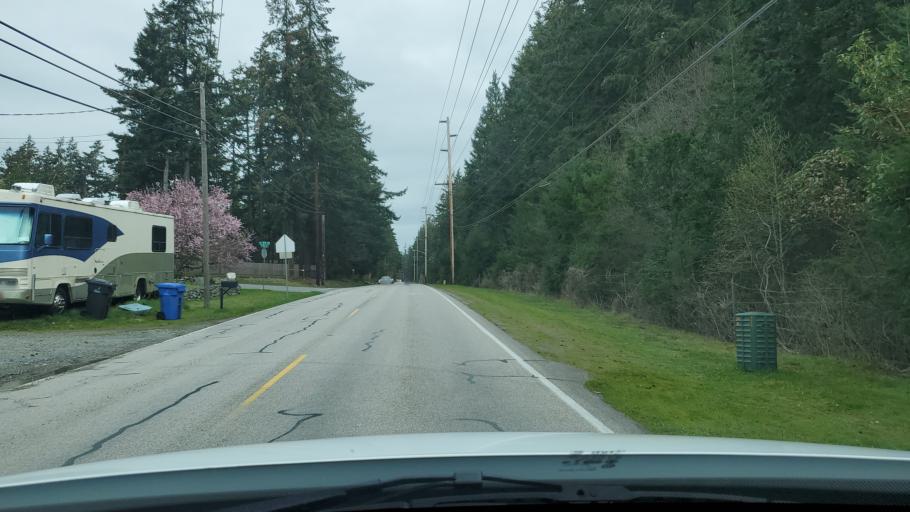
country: US
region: Washington
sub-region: Island County
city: Oak Harbor
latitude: 48.3031
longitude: -122.6334
